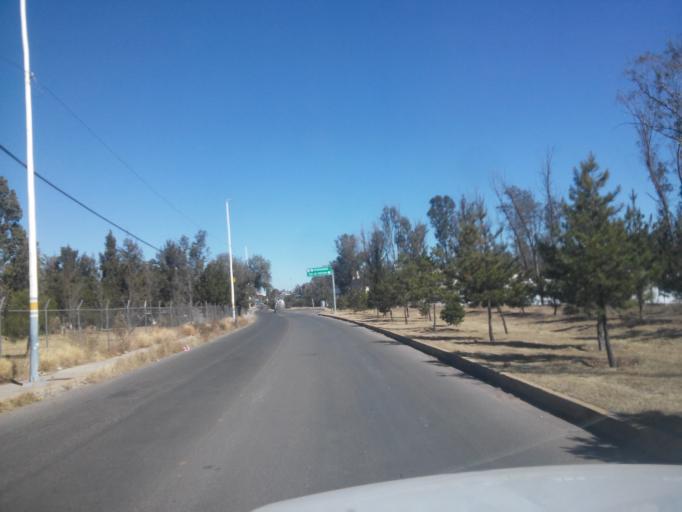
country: MX
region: Durango
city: Victoria de Durango
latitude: 24.0245
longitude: -104.6939
